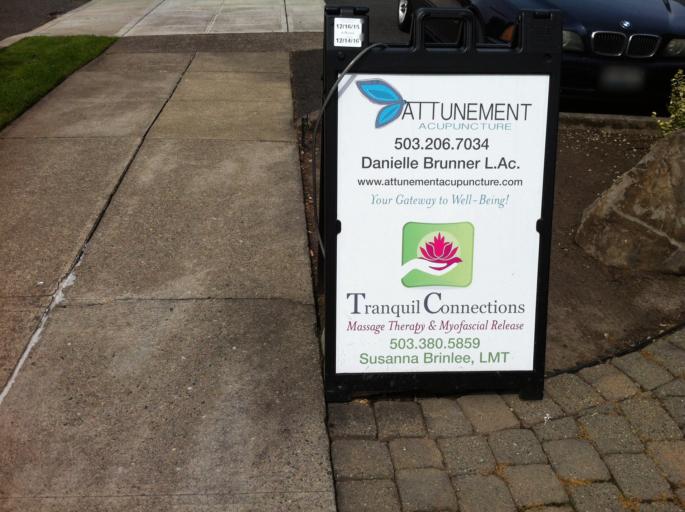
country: US
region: Oregon
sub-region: Multnomah County
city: Portland
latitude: 45.4814
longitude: -122.6757
